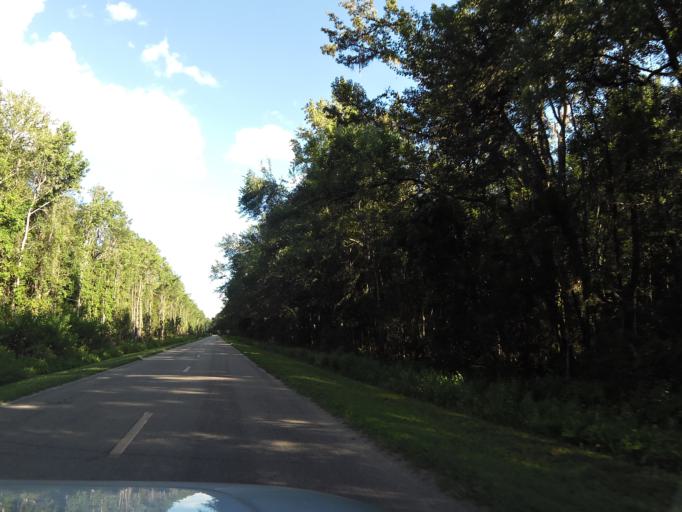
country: US
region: Florida
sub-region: Wakulla County
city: Crawfordville
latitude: 30.0673
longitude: -84.5044
